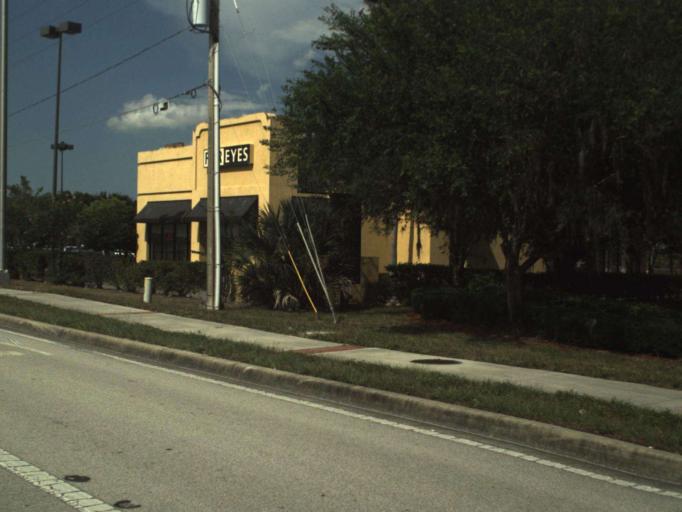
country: US
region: Florida
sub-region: Seminole County
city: Casselberry
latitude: 28.6777
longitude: -81.3361
